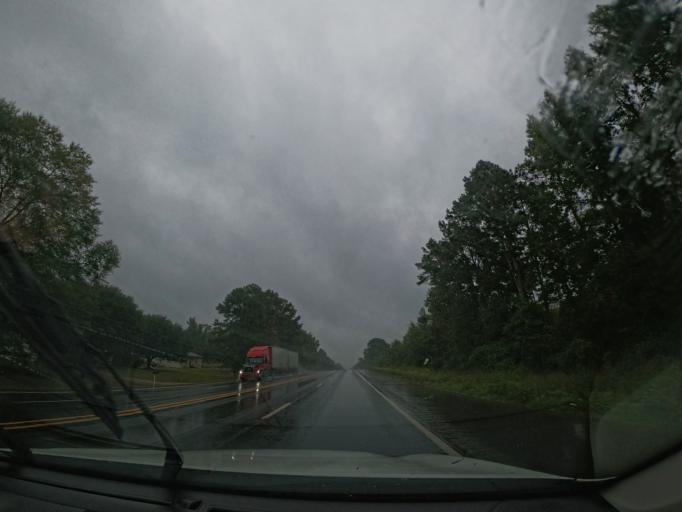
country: US
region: Texas
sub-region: Panola County
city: Carthage
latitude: 32.1618
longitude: -94.3134
